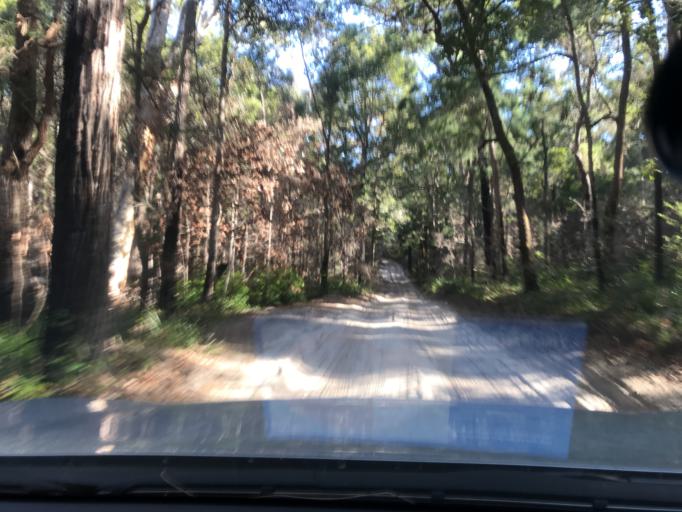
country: AU
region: Queensland
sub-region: Fraser Coast
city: Urangan
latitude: -25.5002
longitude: 153.1013
